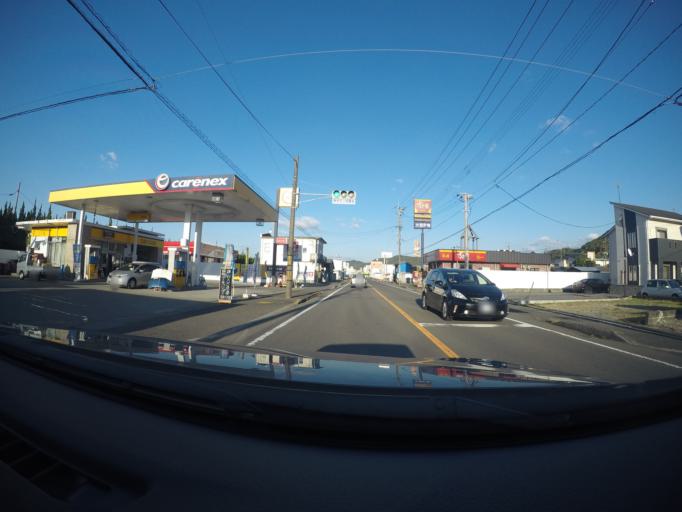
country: JP
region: Kumamoto
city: Minamata
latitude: 32.2030
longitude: 130.3915
